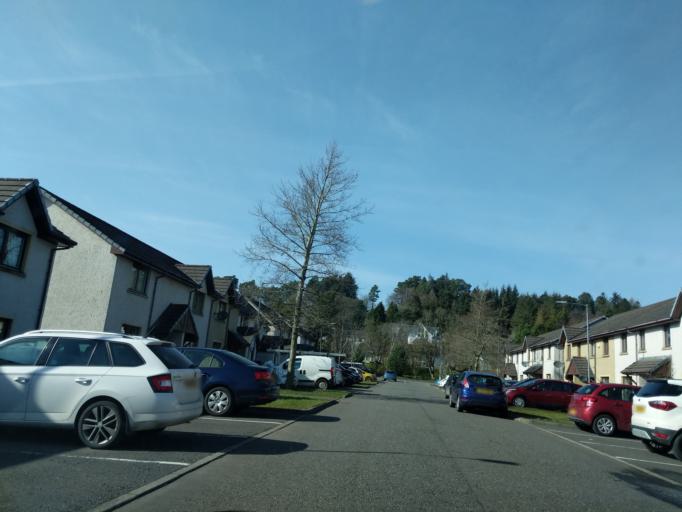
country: GB
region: Scotland
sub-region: The Scottish Borders
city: West Linton
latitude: 55.7538
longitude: -3.3499
